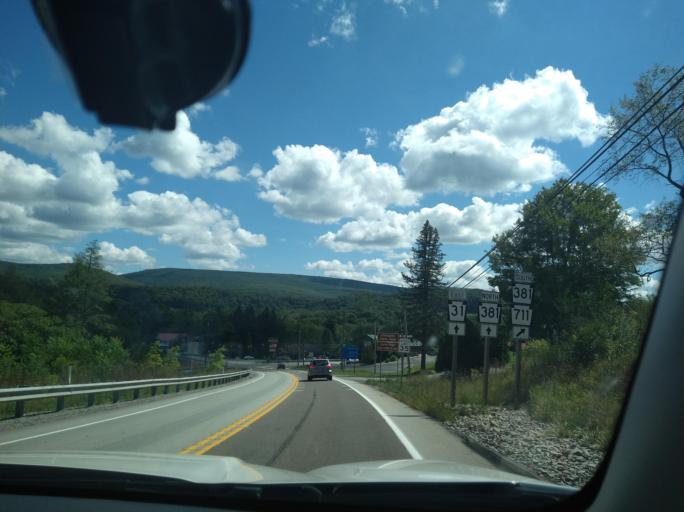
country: US
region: Pennsylvania
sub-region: Fayette County
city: Bear Rocks
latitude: 40.0923
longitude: -79.3493
